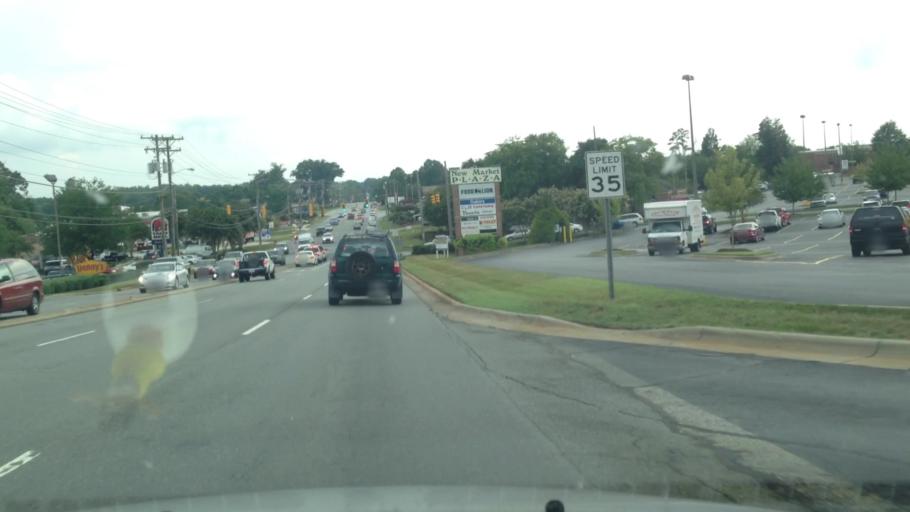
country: US
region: North Carolina
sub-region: Forsyth County
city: Kernersville
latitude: 36.1092
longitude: -80.0945
